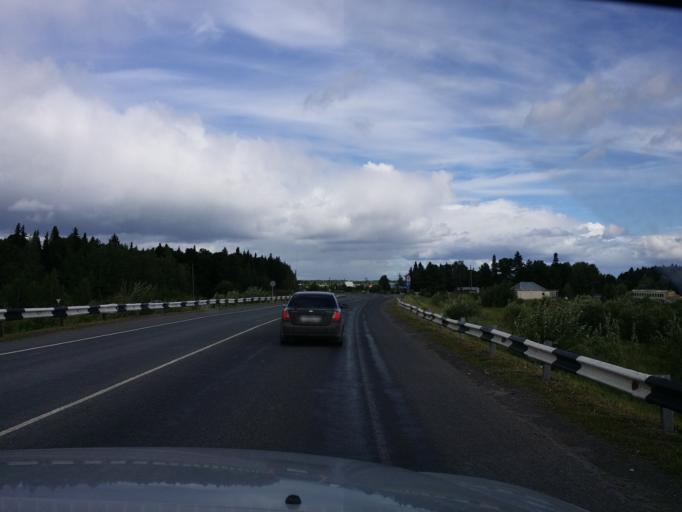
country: RU
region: Tjumen
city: Tobol'sk
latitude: 58.3344
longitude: 68.3241
